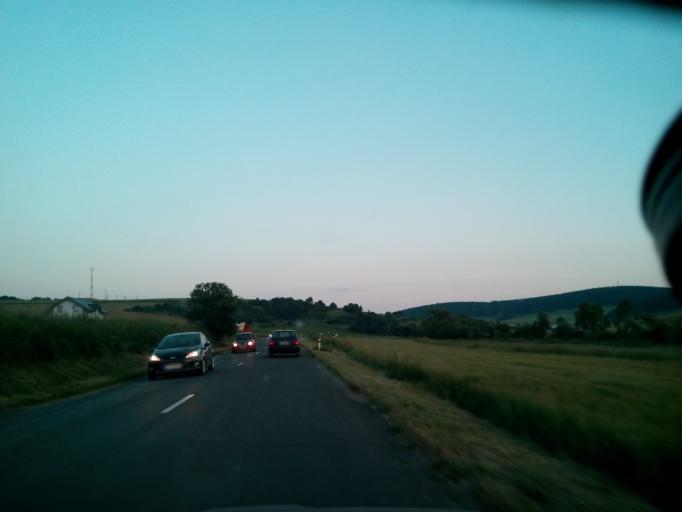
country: SK
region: Presovsky
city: Lubica
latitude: 49.0688
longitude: 20.4331
